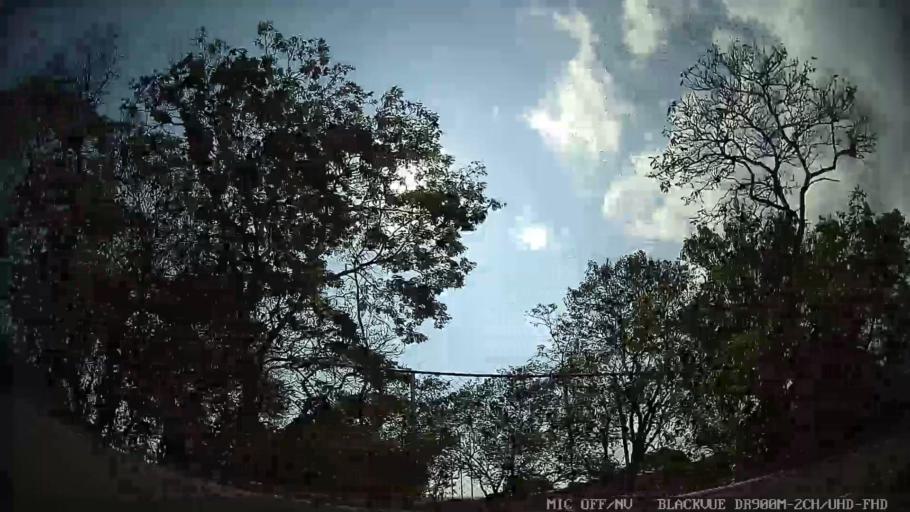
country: BR
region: Sao Paulo
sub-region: Ferraz De Vasconcelos
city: Ferraz de Vasconcelos
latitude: -23.5011
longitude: -46.4482
